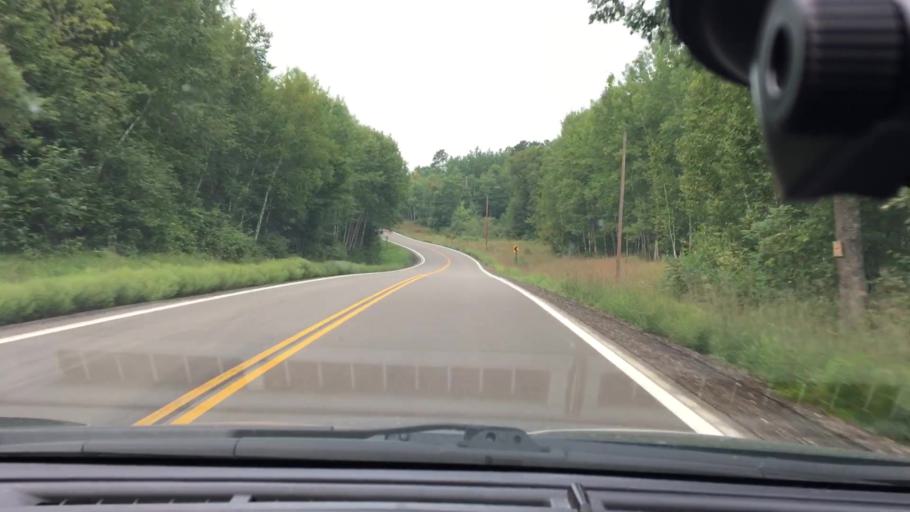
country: US
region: Minnesota
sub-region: Crow Wing County
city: Cross Lake
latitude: 46.6591
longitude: -93.9685
